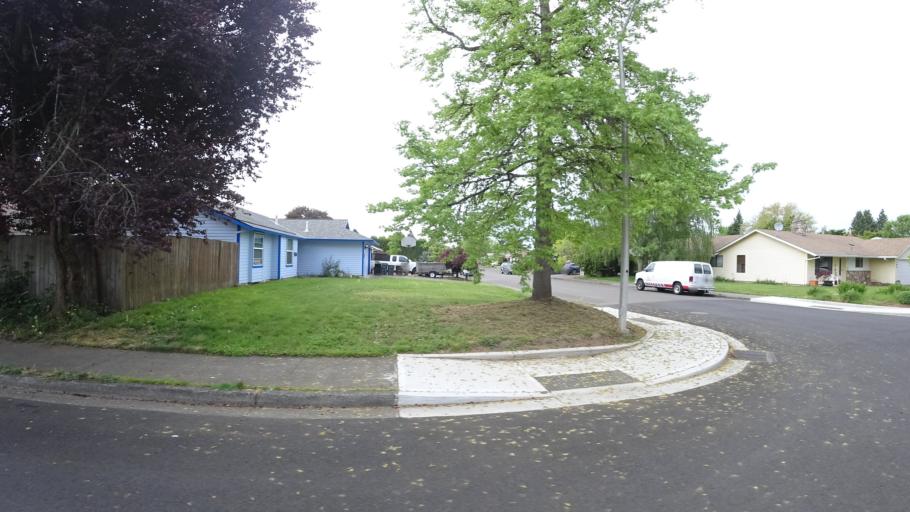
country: US
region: Oregon
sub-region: Washington County
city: Hillsboro
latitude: 45.4957
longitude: -122.9651
